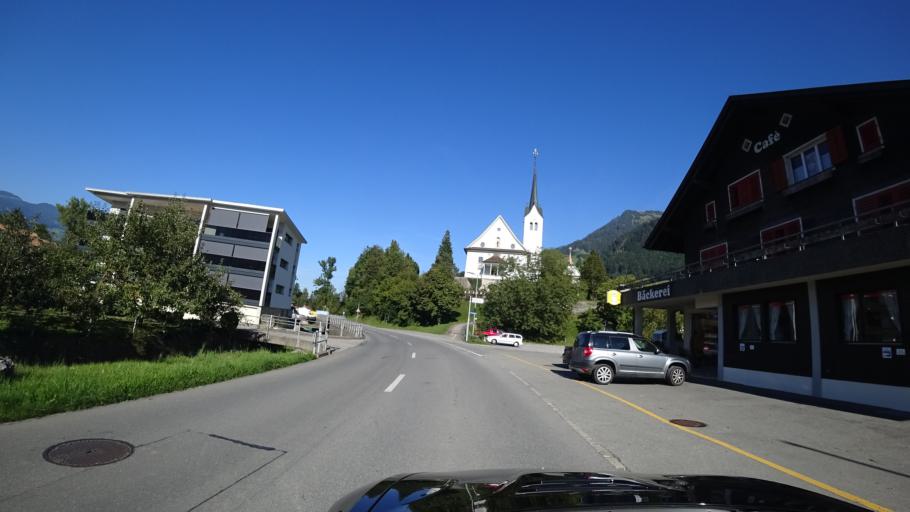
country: CH
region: Obwalden
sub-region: Obwalden
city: Giswil
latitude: 46.8313
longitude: 8.1771
